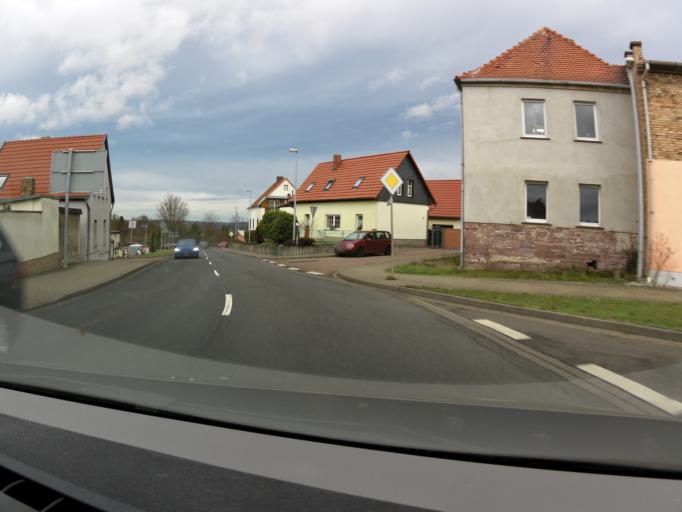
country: DE
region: Saxony-Anhalt
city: Mansfeld
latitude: 51.5646
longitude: 11.4271
